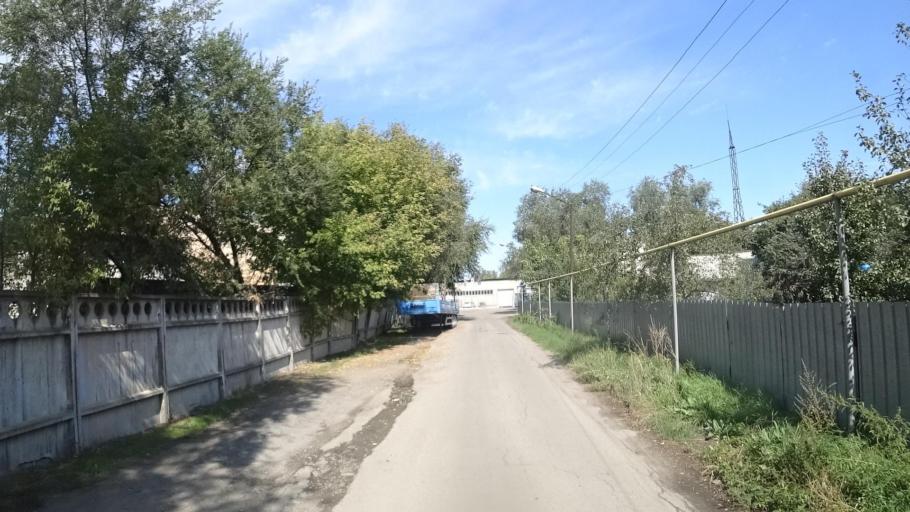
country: KZ
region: Almaty Oblysy
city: Pervomayskiy
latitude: 43.3319
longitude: 76.9749
